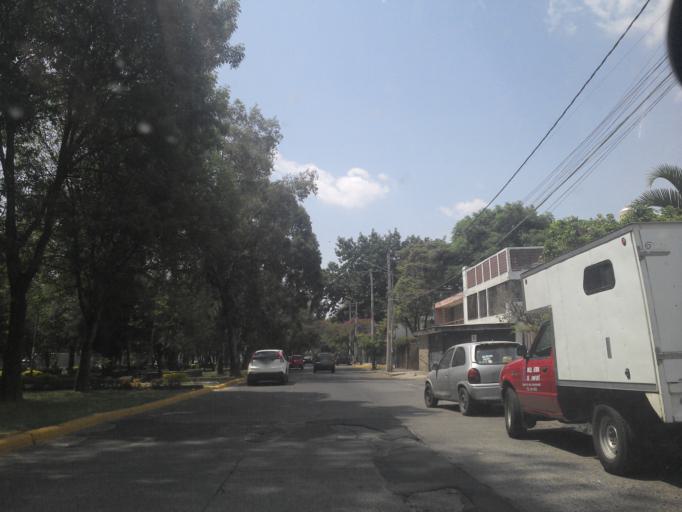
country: MX
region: Jalisco
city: Guadalajara
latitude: 20.6614
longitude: -103.3856
